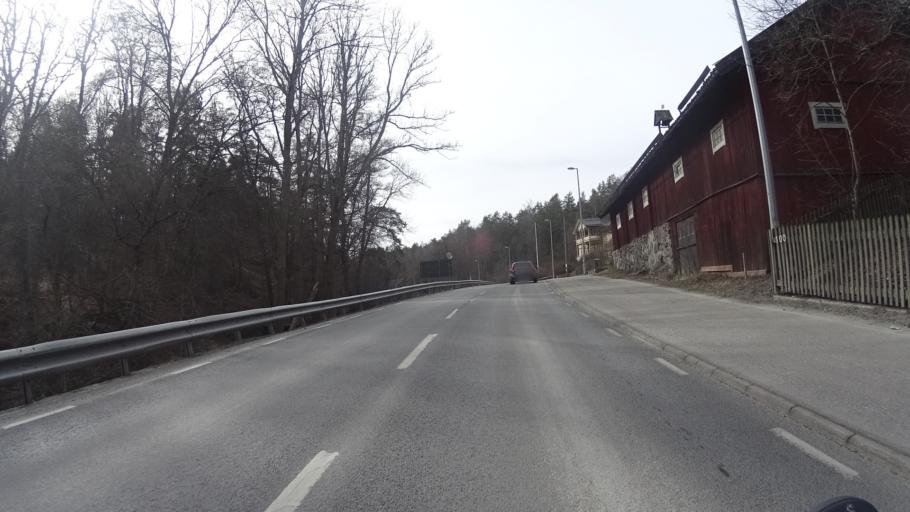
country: SE
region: Stockholm
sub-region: Nacka Kommun
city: Nacka
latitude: 59.2988
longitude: 18.1480
